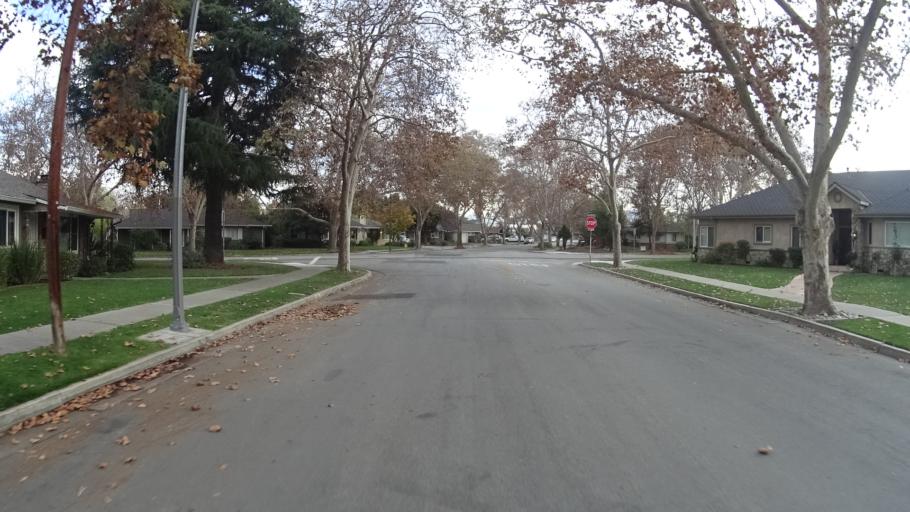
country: US
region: California
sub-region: Santa Clara County
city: Buena Vista
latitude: 37.3256
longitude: -121.9202
